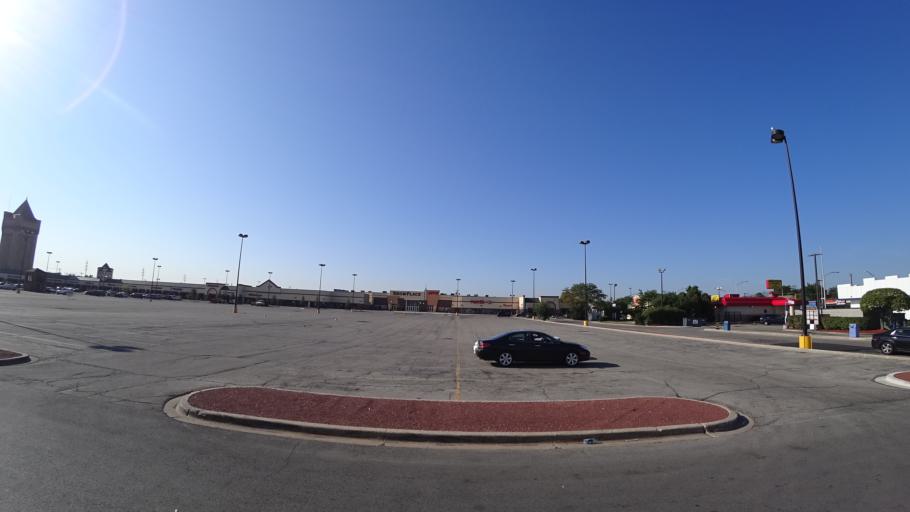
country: US
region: Illinois
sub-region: Cook County
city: Cicero
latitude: 41.8505
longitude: -87.7432
